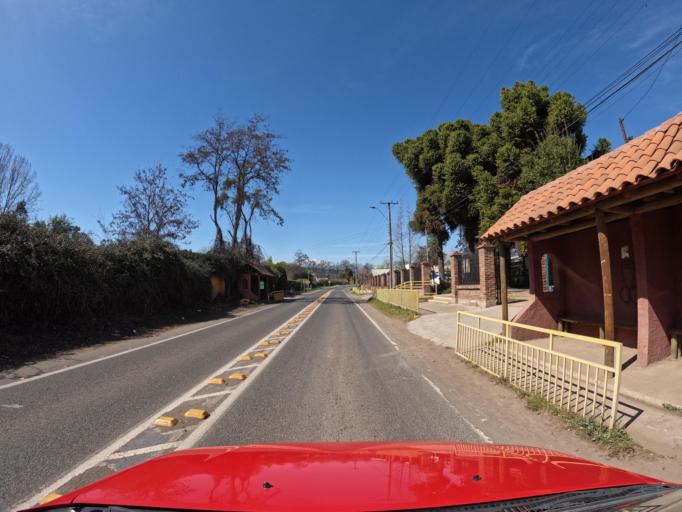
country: CL
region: Maule
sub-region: Provincia de Curico
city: Teno
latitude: -34.9689
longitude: -71.0131
